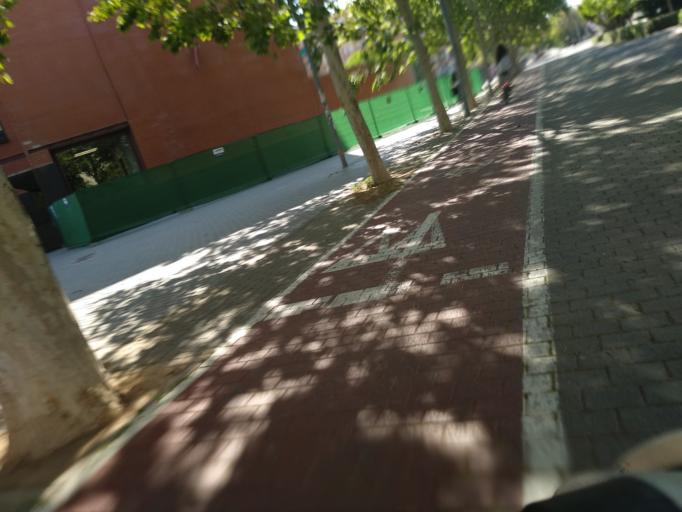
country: ES
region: Valencia
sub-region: Provincia de Valencia
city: Alboraya
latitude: 39.4777
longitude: -0.3450
